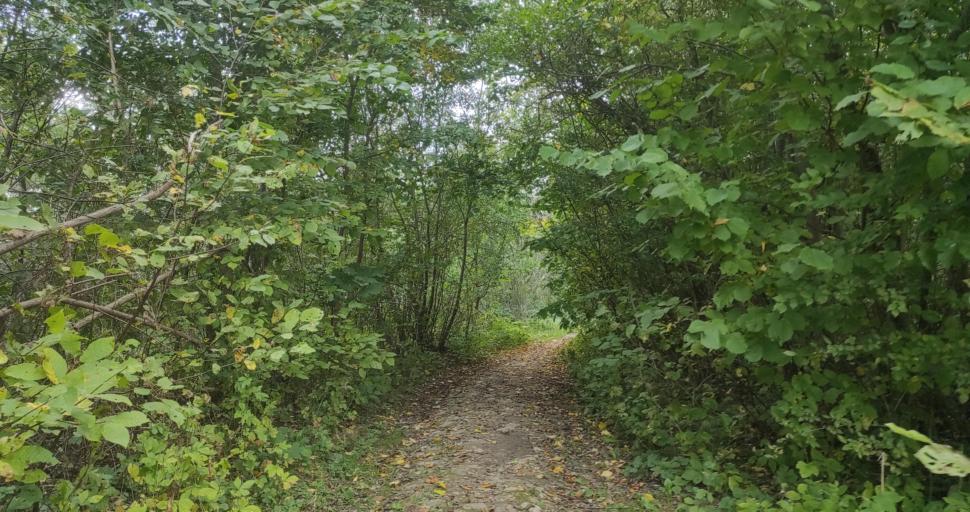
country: LV
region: Kuldigas Rajons
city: Kuldiga
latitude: 56.9917
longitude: 21.9583
